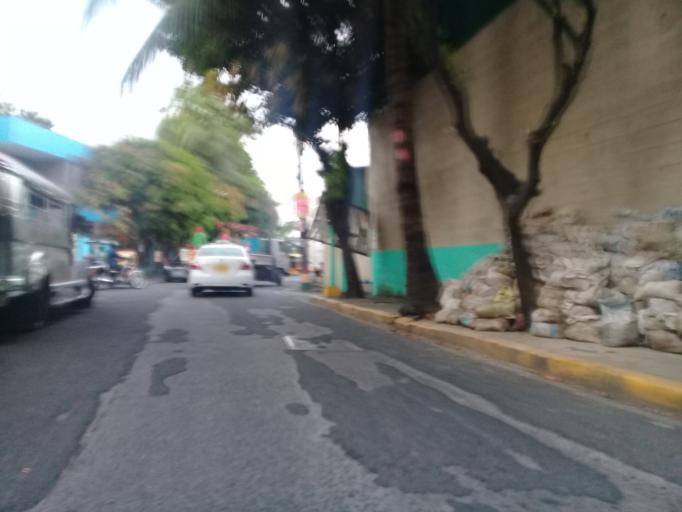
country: PH
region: Metro Manila
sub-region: Mandaluyong
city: Mandaluyong City
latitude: 14.5797
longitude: 121.0159
